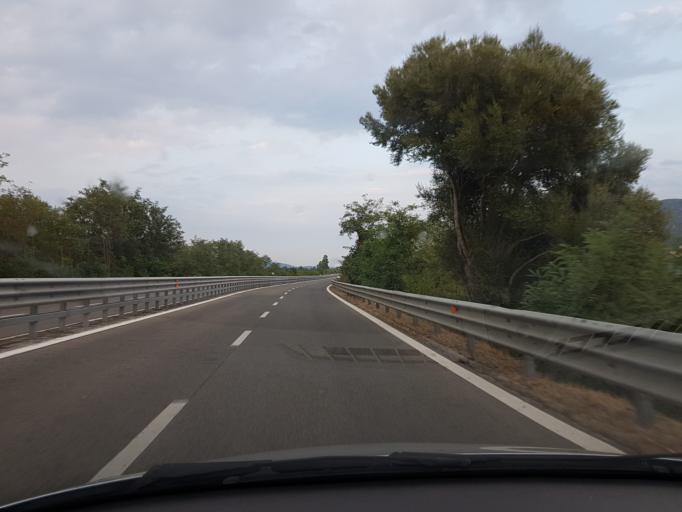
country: IT
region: Sardinia
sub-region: Provincia di Nuoro
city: Orune
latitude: 40.3782
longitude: 9.4209
